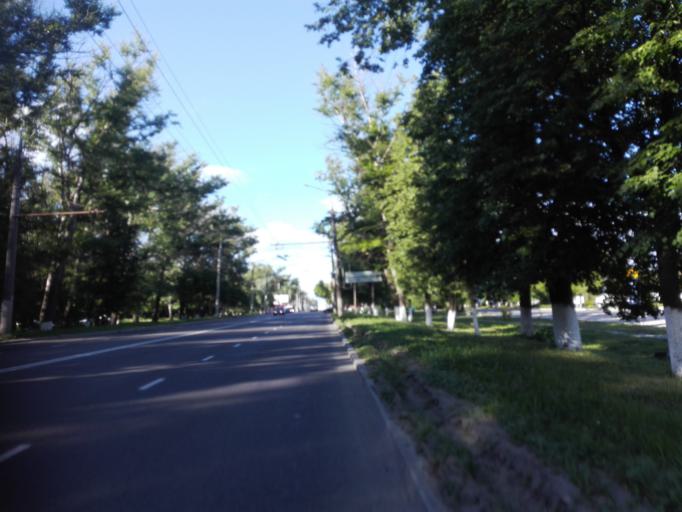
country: RU
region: Orjol
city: Orel
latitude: 53.0064
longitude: 36.1473
